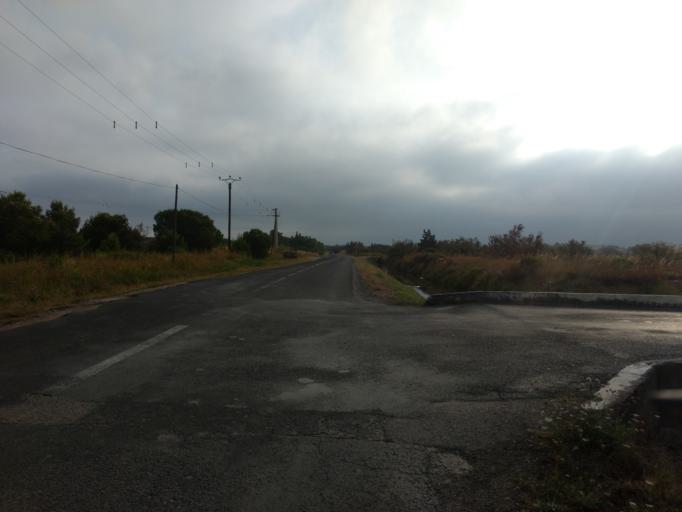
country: FR
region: Languedoc-Roussillon
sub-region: Departement des Pyrenees-Orientales
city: Le Barcares
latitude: 42.7885
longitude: 3.0231
